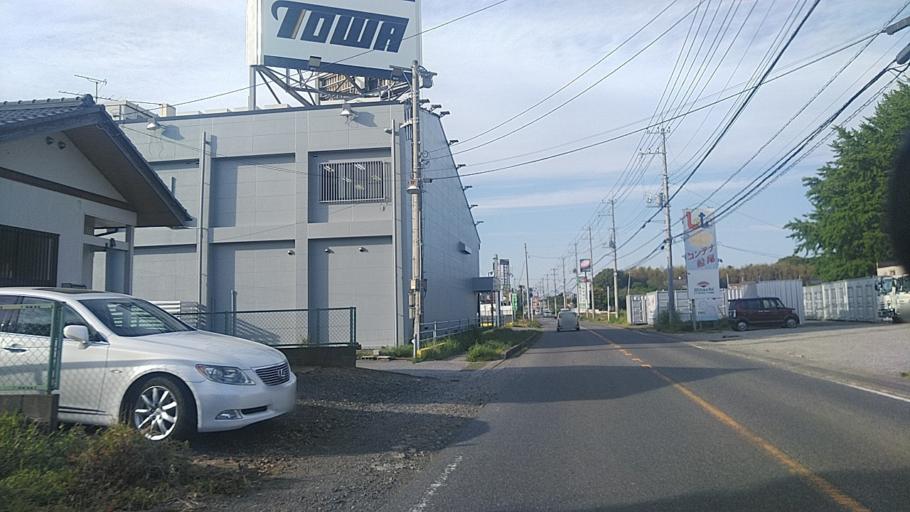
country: JP
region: Chiba
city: Shiroi
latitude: 35.7881
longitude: 140.1303
